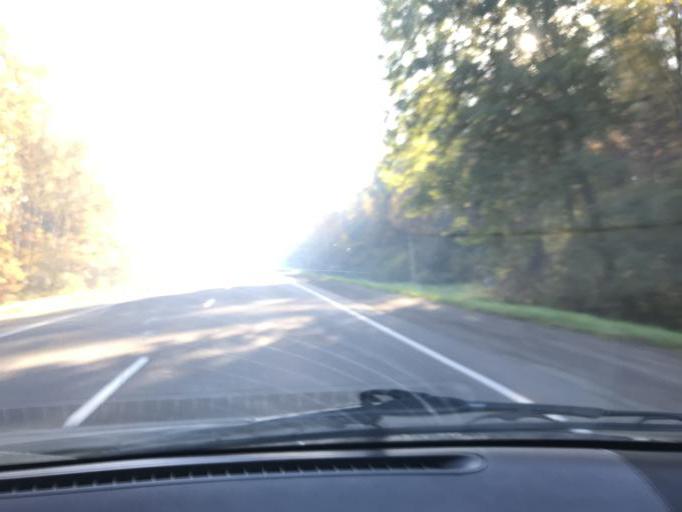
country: BY
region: Brest
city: Horad Luninyets
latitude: 52.2910
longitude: 26.7722
